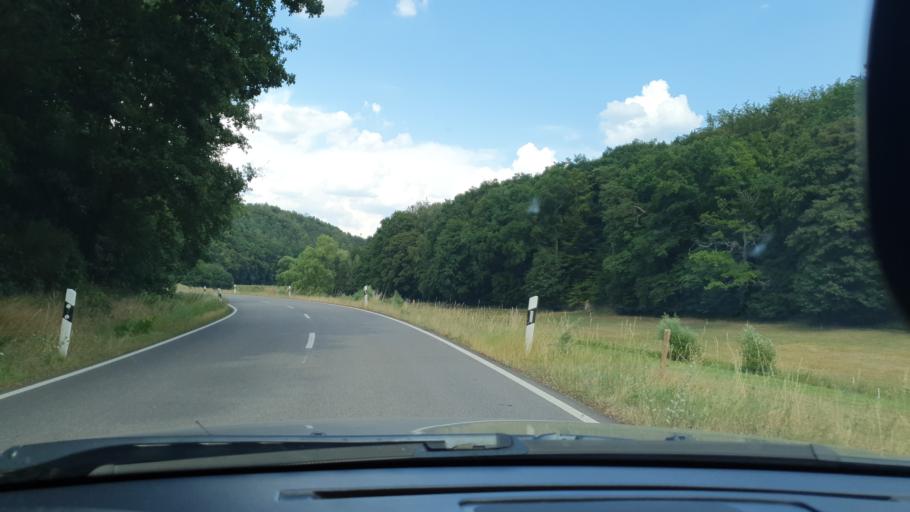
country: DE
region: Rheinland-Pfalz
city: Bechhofen
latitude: 49.3592
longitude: 7.4121
